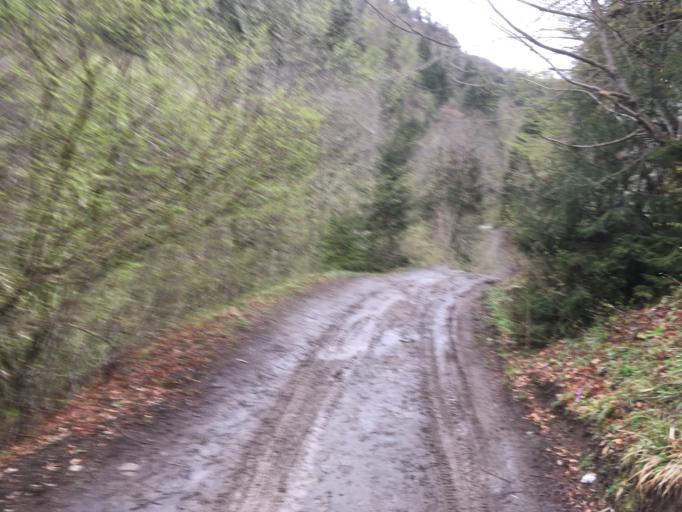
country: GE
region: Samtskhe-Javakheti
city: Borjomi
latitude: 41.8204
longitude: 43.3986
